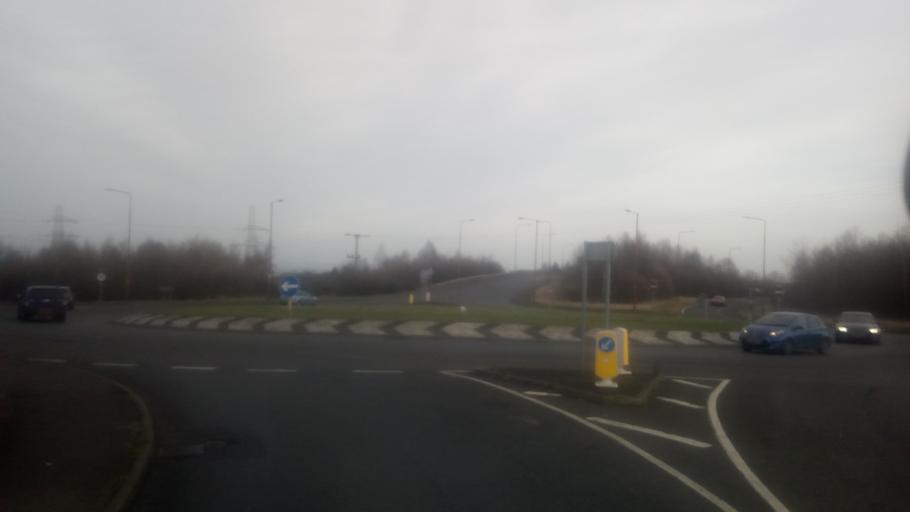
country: GB
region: Scotland
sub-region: East Lothian
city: Tranent
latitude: 55.9509
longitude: -2.9555
